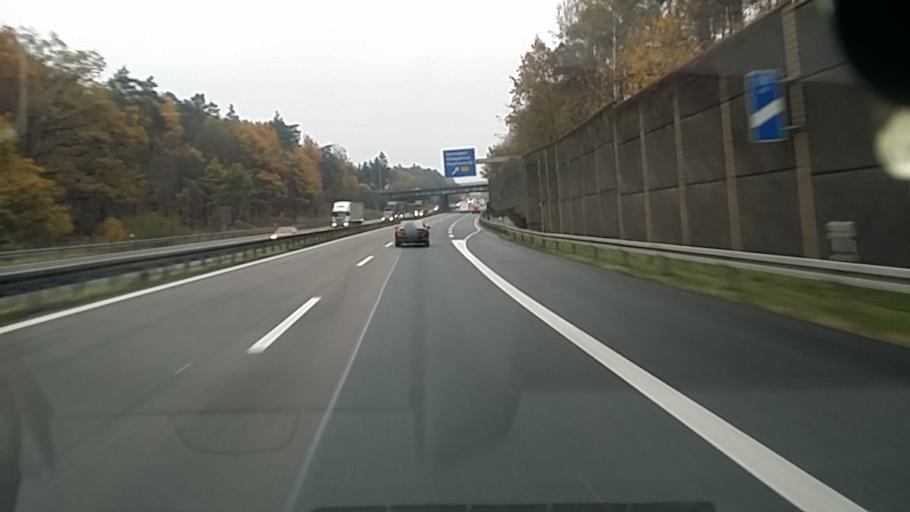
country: DE
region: Saxony
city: Ottendorf-Okrilla
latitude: 51.1722
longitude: 13.8194
